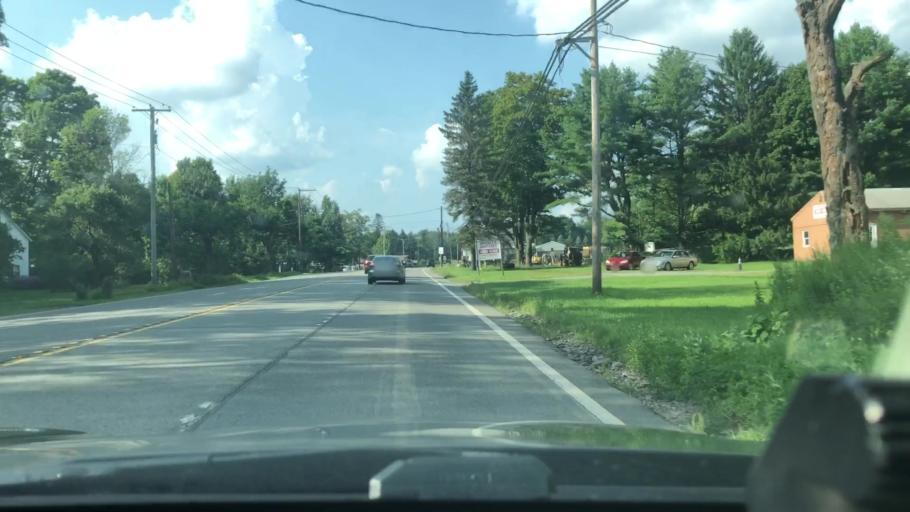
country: US
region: Pennsylvania
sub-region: Lackawanna County
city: Moscow
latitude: 41.2666
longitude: -75.5071
